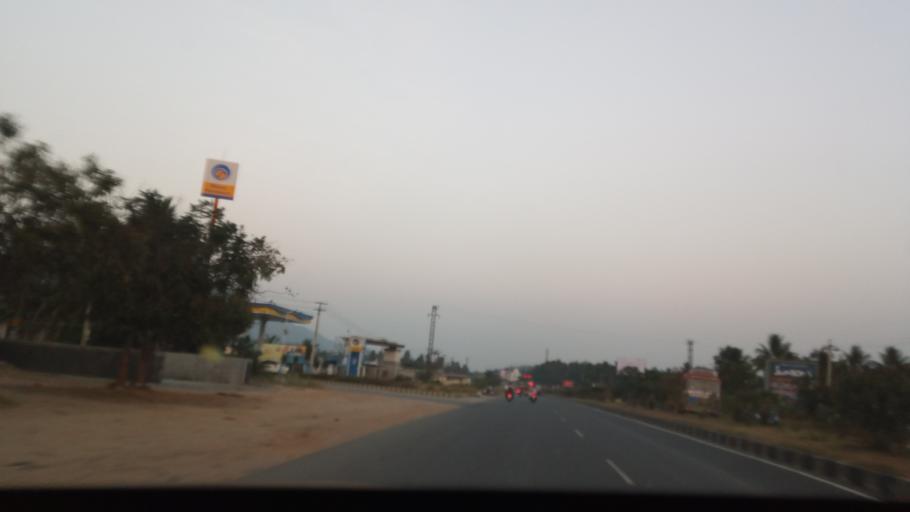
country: IN
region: Tamil Nadu
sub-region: Salem
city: Belur
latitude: 11.6647
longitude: 78.3065
